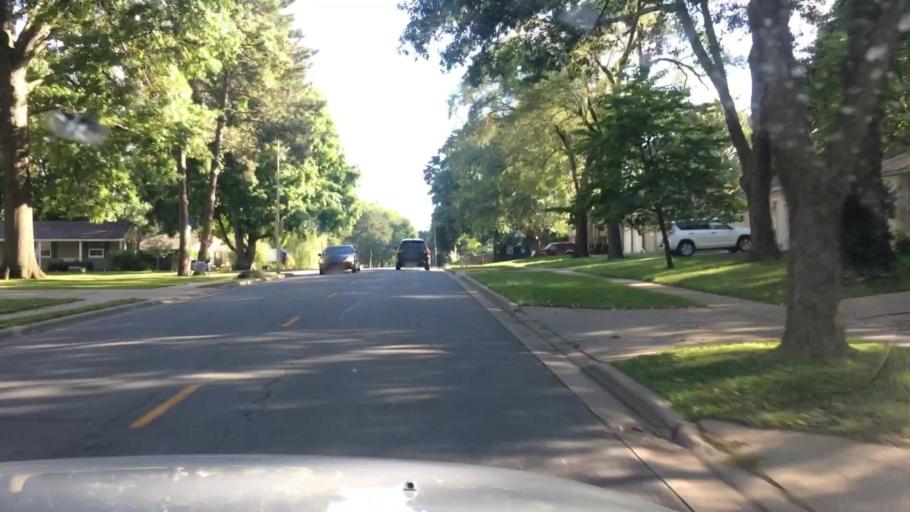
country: US
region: Kansas
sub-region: Johnson County
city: Overland Park
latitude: 38.9906
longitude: -94.6584
